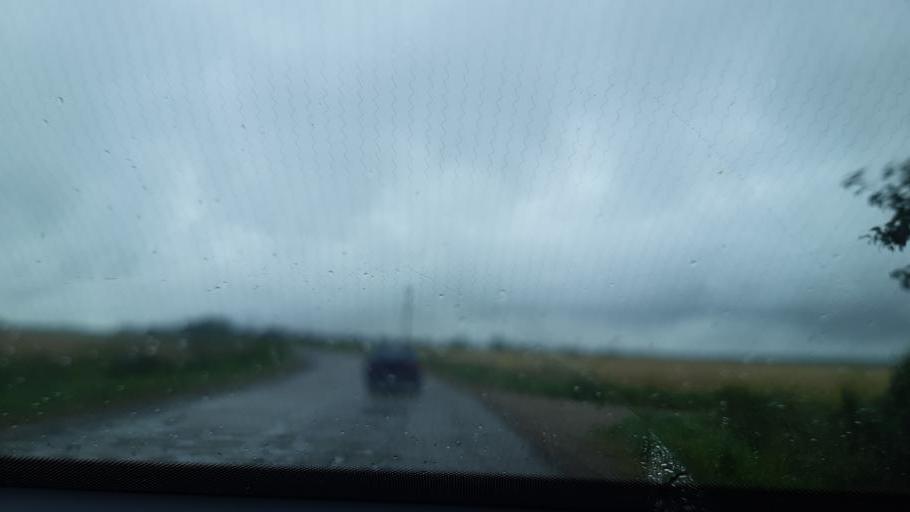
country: RU
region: Smolensk
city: Gagarin
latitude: 55.6365
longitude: 34.7543
